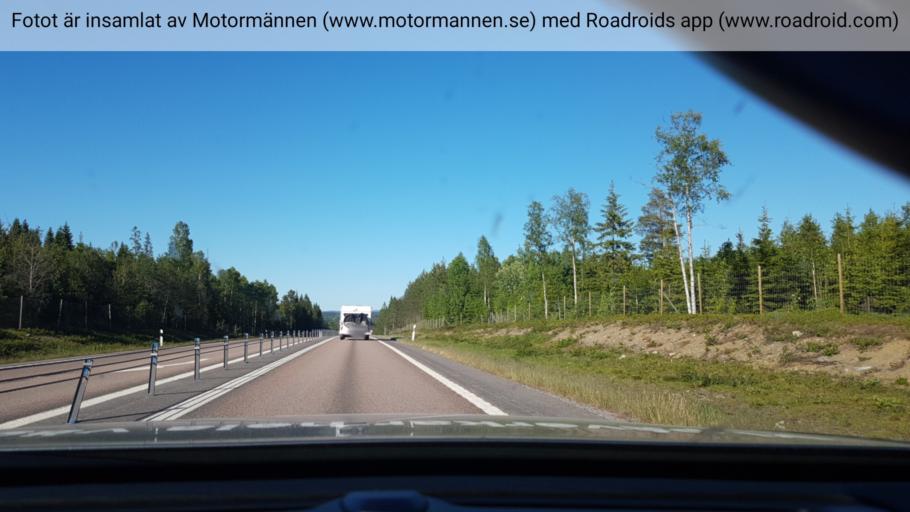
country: SE
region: Vaesternorrland
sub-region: Haernoesands Kommun
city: Haernoesand
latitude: 62.5690
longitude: 17.7386
